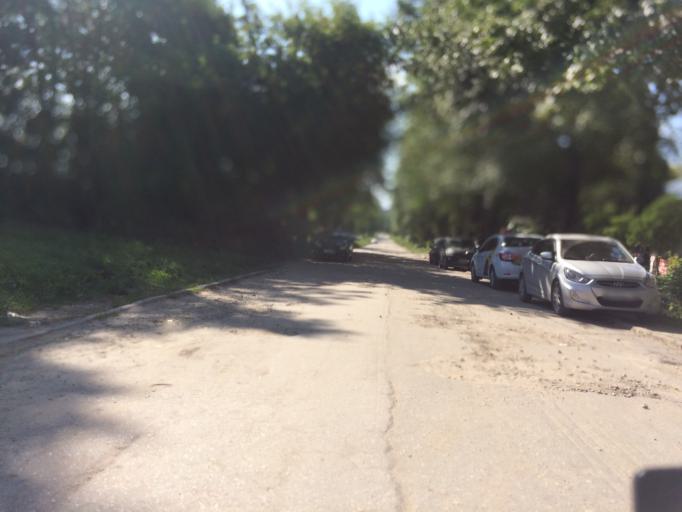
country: RU
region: Mariy-El
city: Yoshkar-Ola
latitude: 56.6289
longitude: 47.9451
